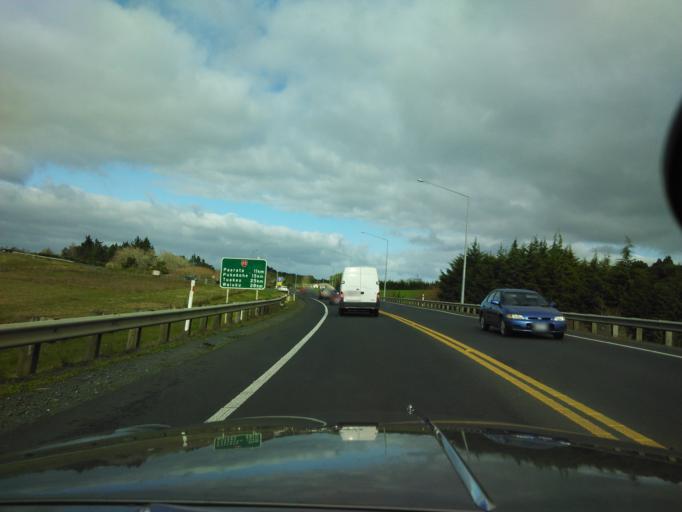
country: NZ
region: Auckland
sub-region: Auckland
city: Papakura
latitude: -37.1107
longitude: 174.9427
